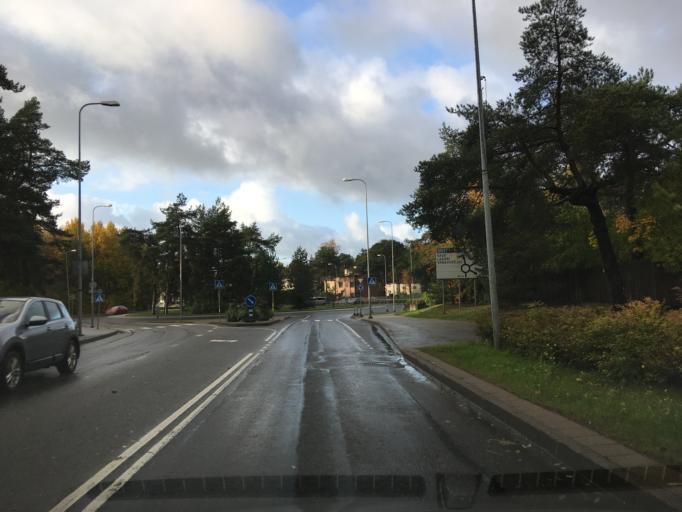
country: EE
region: Harju
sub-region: Saue vald
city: Laagri
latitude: 59.3650
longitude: 24.6308
